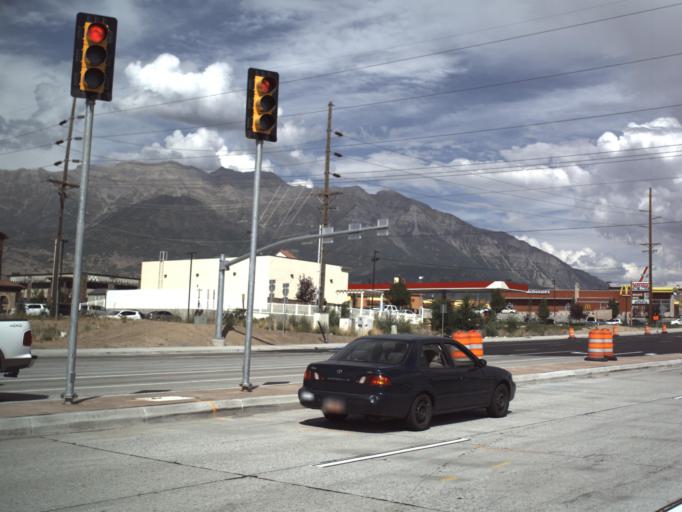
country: US
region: Utah
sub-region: Utah County
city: Lindon
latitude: 40.3117
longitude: -111.7278
